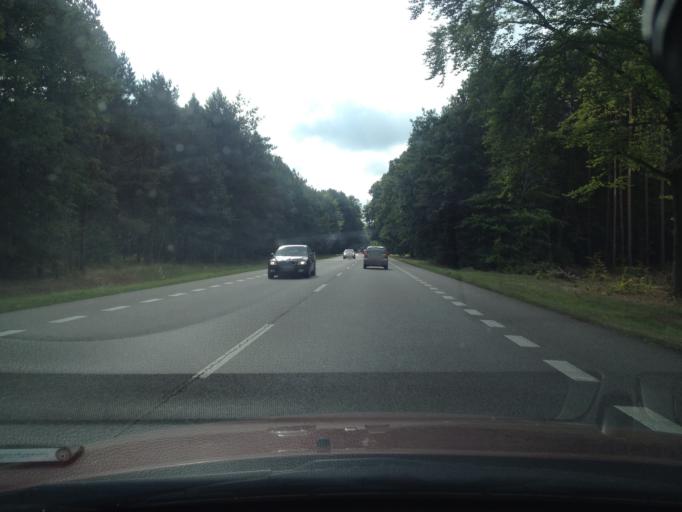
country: PL
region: West Pomeranian Voivodeship
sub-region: Powiat goleniowski
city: Przybiernow
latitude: 53.6922
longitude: 14.7936
